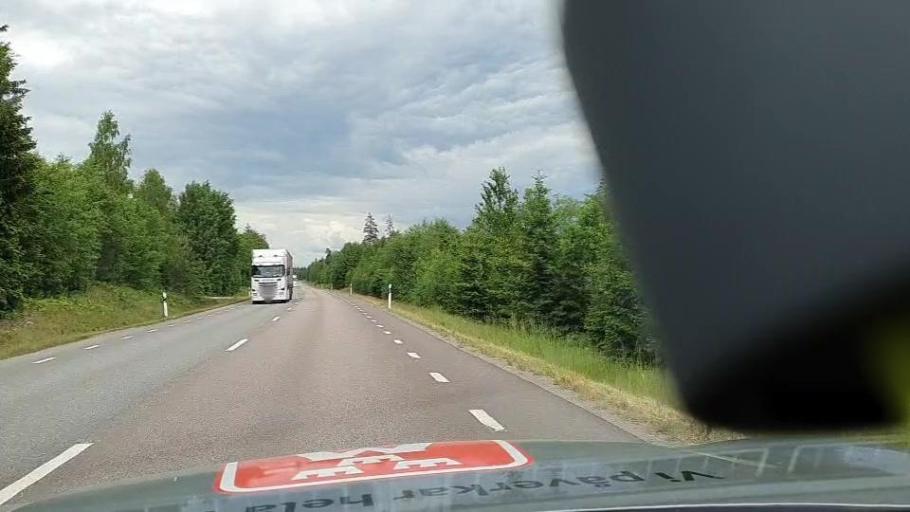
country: SE
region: Kalmar
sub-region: Emmaboda Kommun
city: Emmaboda
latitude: 56.4434
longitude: 15.5574
